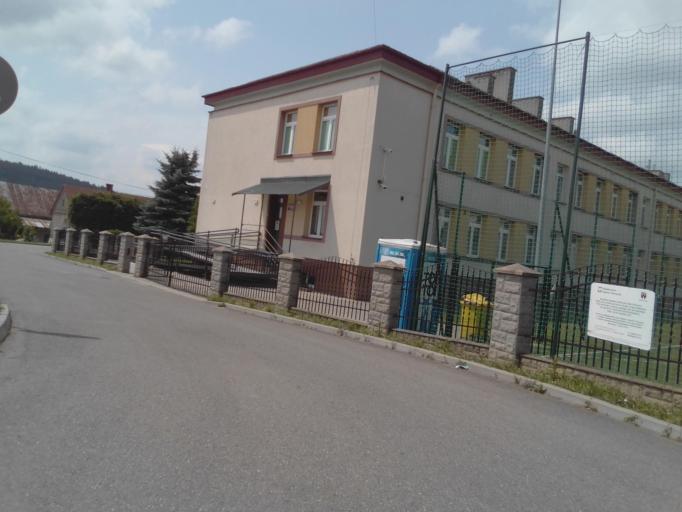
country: PL
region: Subcarpathian Voivodeship
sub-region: Powiat strzyzowski
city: Czudec
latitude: 49.9446
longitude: 21.8444
